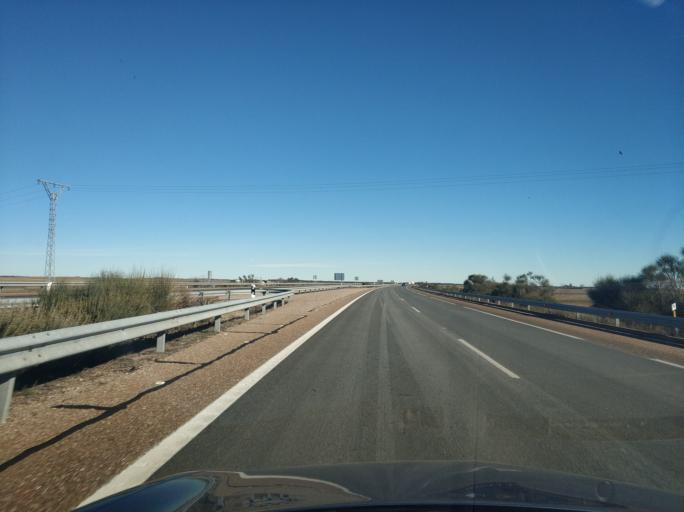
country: ES
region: Castille and Leon
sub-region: Provincia de Salamanca
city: Pajares de la Laguna
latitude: 41.0985
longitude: -5.4998
